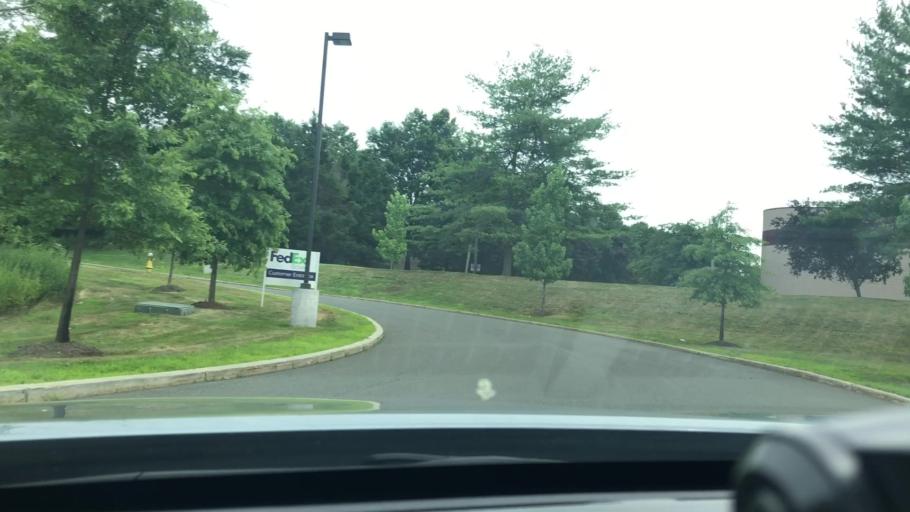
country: US
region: New York
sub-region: Rockland County
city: Blauvelt
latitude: 41.0807
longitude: -73.9538
